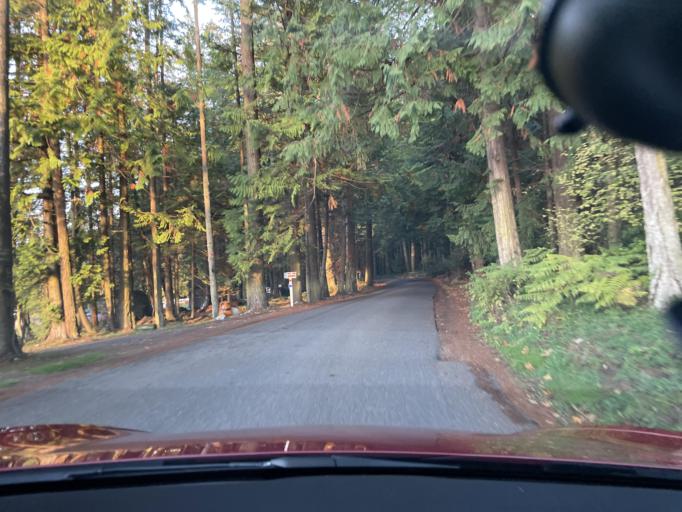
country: US
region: Washington
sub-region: San Juan County
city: Friday Harbor
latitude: 48.6145
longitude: -123.1541
